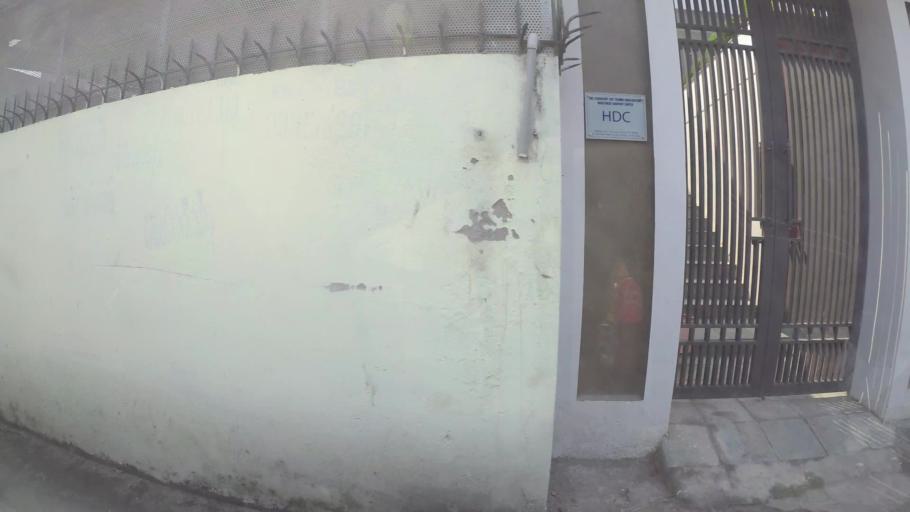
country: VN
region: Ha Noi
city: Ha Dong
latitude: 21.0007
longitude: 105.7574
